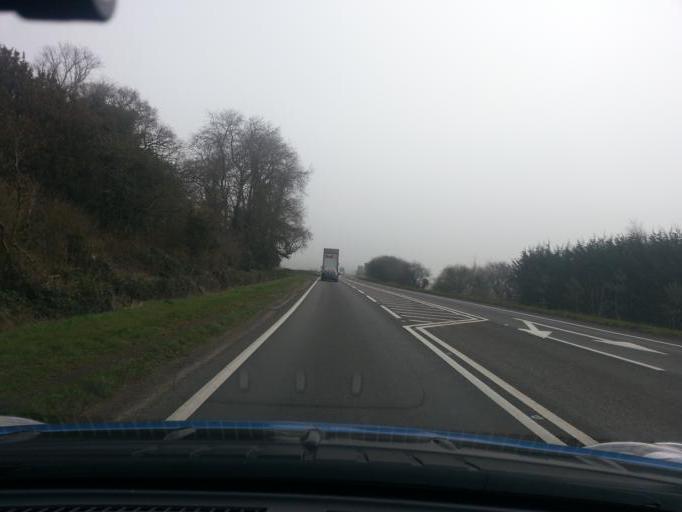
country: GB
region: England
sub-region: Oxfordshire
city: Stanford in the Vale
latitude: 51.6741
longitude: -1.5269
